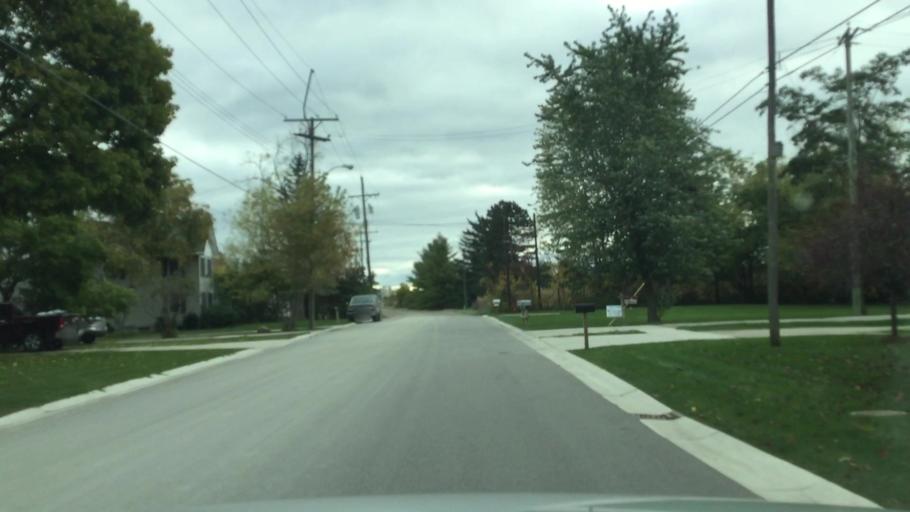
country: US
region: Michigan
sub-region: Macomb County
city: Richmond
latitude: 42.8222
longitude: -82.7508
